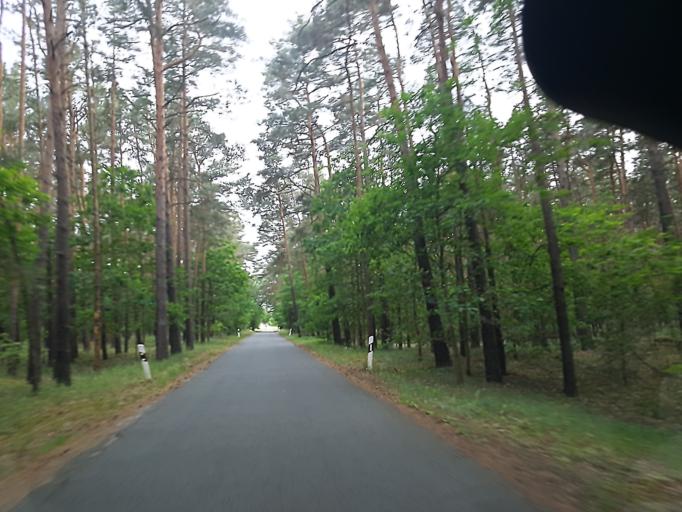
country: DE
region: Saxony-Anhalt
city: Holzdorf
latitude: 51.7682
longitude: 13.1072
